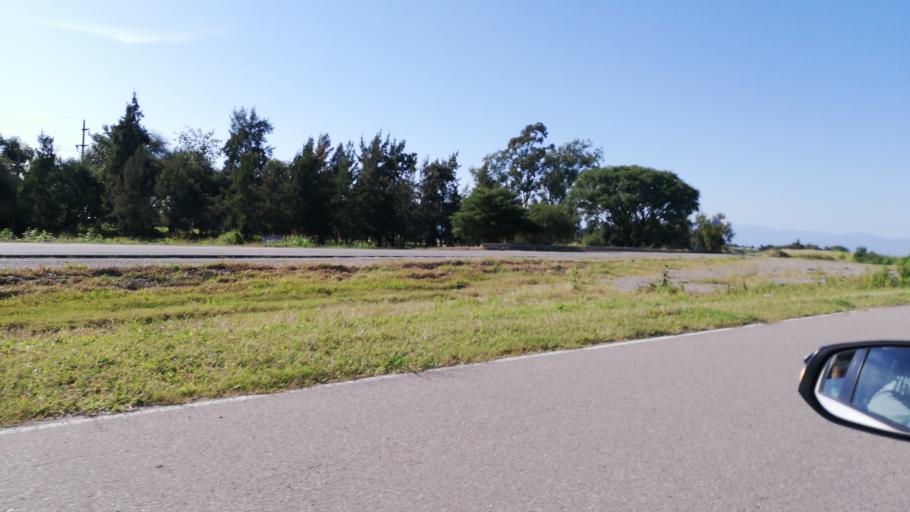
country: AR
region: Jujuy
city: La Mendieta
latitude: -24.3939
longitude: -65.0860
